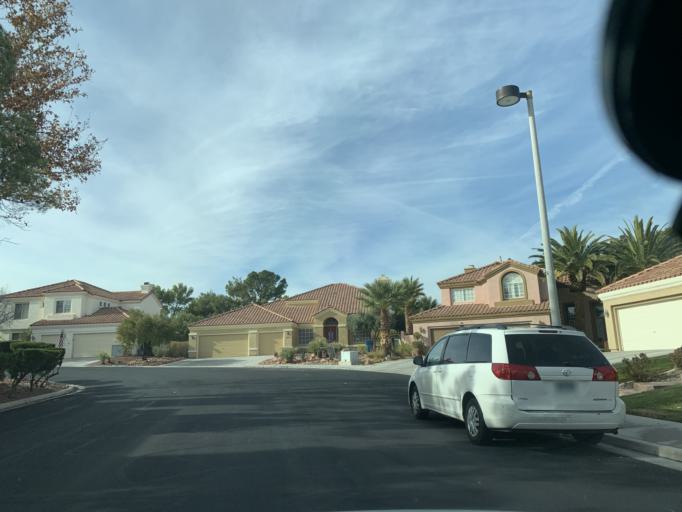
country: US
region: Nevada
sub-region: Clark County
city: Summerlin South
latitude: 36.1539
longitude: -115.3015
